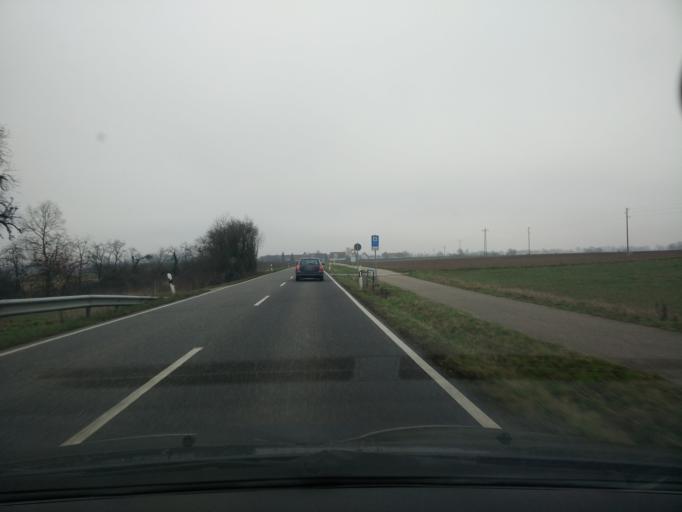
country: DE
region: Rheinland-Pfalz
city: Hergersweiler
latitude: 49.0962
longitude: 8.1010
